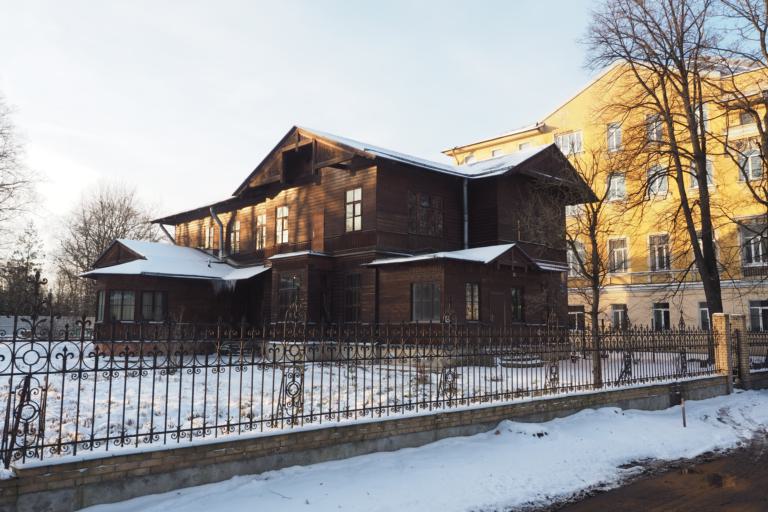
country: RU
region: St.-Petersburg
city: Novaya Derevnya
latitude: 59.9796
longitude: 30.2813
